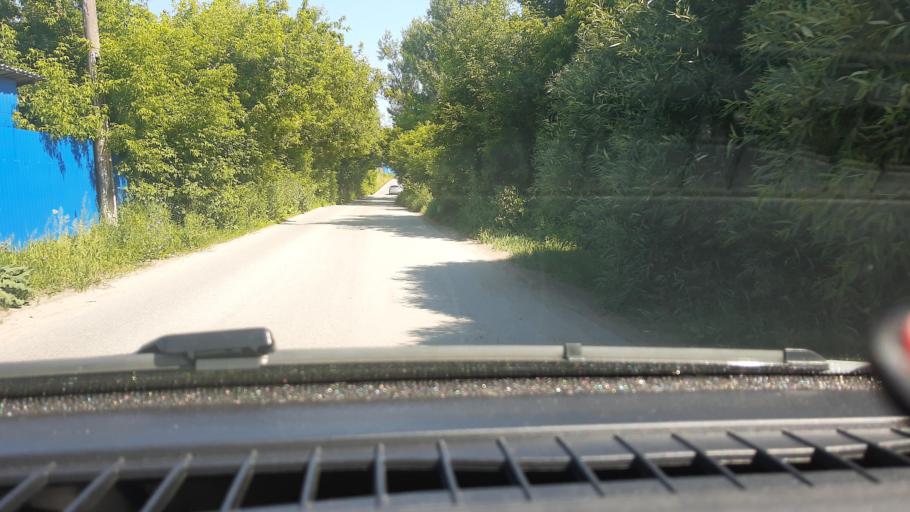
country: RU
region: Nizjnij Novgorod
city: Afonino
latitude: 56.2748
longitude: 44.1920
